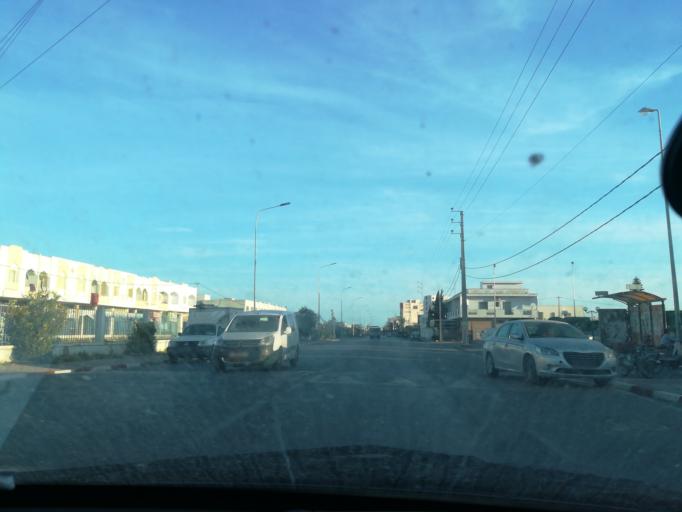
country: TN
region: Safaqis
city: Al Qarmadah
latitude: 34.8125
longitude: 10.7618
